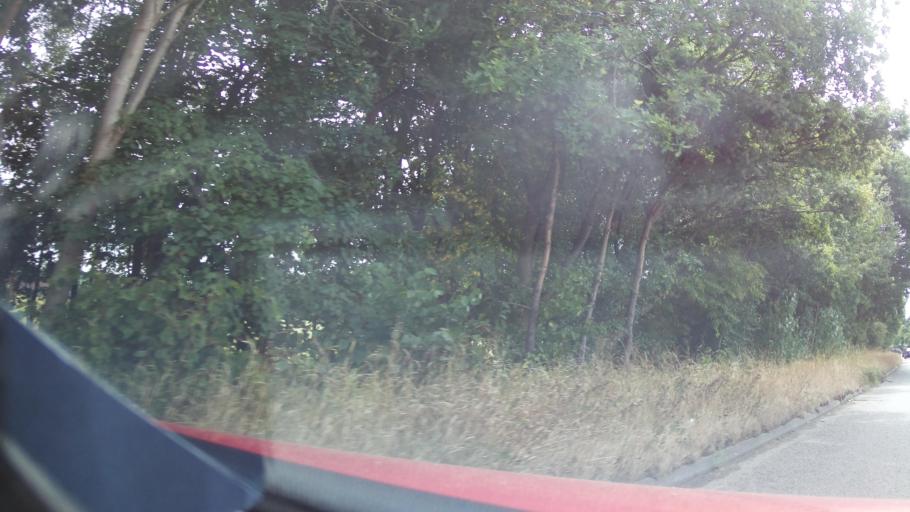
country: GB
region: England
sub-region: Derby
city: Derby
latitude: 52.9307
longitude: -1.4657
